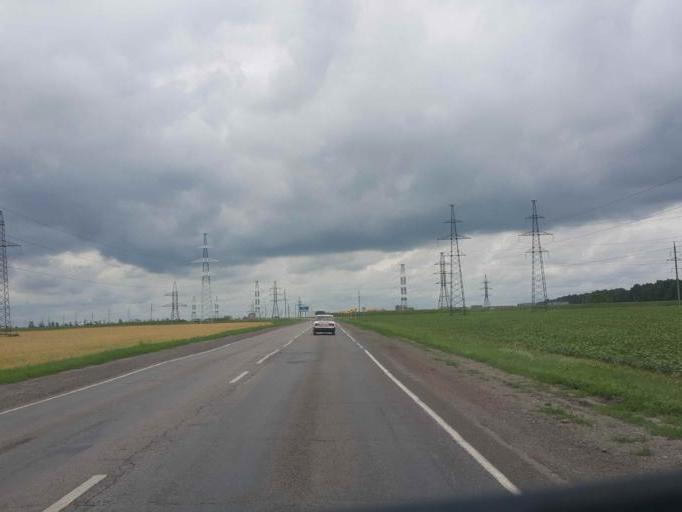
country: RU
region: Tambov
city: Komsomolets
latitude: 52.7791
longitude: 41.3474
